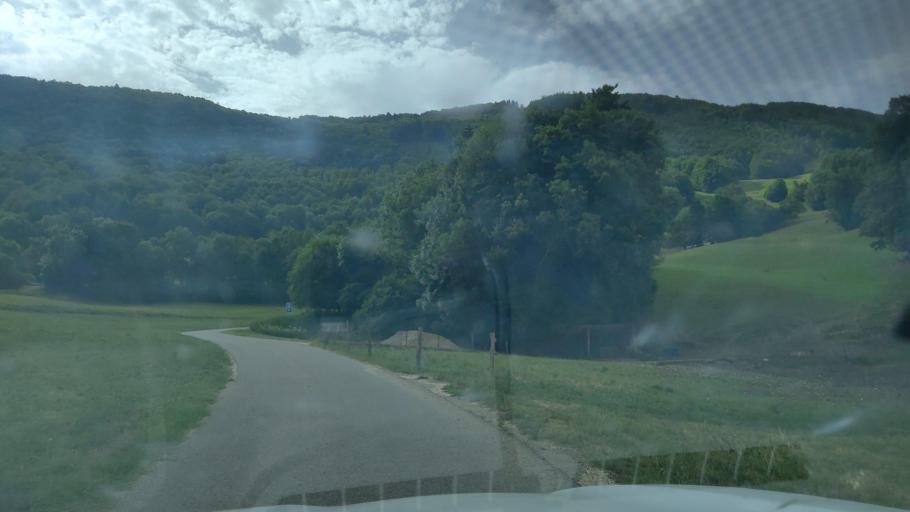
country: FR
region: Rhone-Alpes
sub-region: Departement de la Savoie
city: Cruet
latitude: 45.6095
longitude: 6.1105
